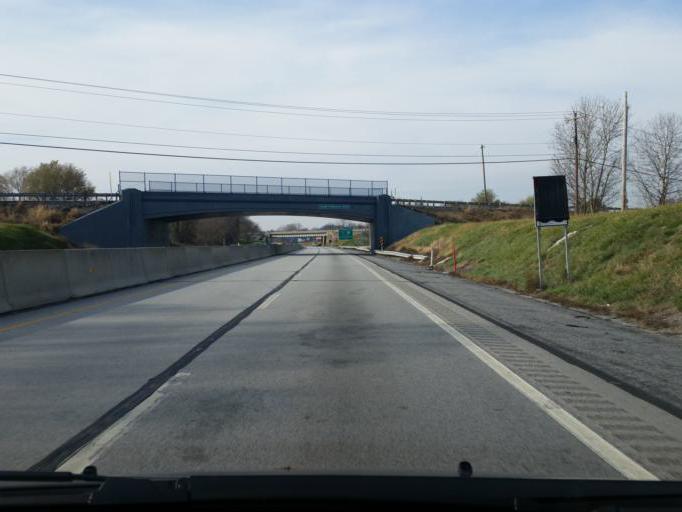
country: US
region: Pennsylvania
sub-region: Cumberland County
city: Schlusser
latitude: 40.2278
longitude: -77.1297
